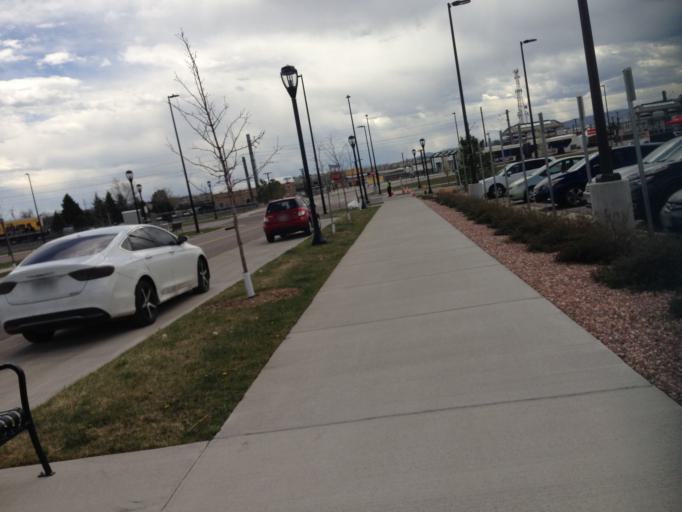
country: US
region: Colorado
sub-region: Jefferson County
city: Applewood
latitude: 39.7893
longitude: -105.1326
